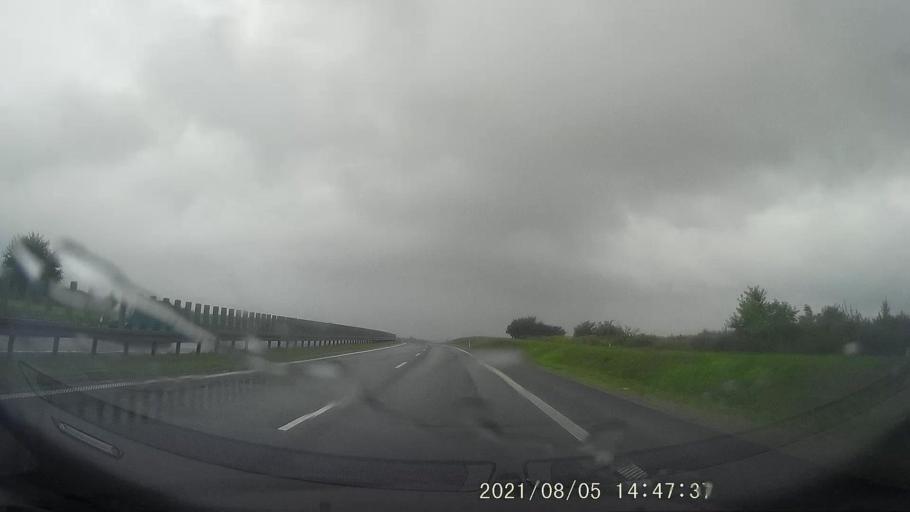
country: PL
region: Opole Voivodeship
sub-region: Powiat nyski
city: Nysa
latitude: 50.5008
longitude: 17.3098
